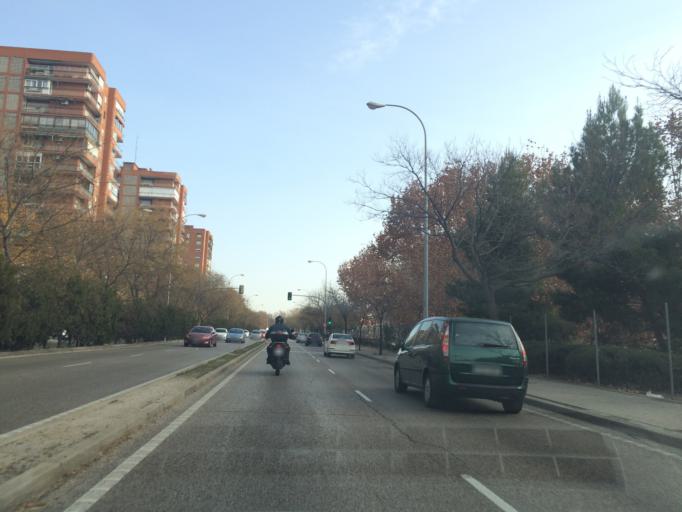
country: ES
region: Madrid
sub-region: Provincia de Madrid
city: Tetuan de las Victorias
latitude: 40.4716
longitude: -3.7081
